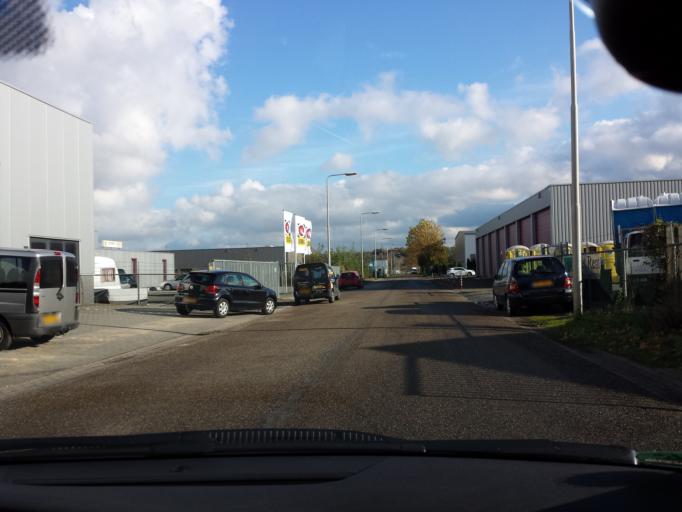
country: NL
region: Limburg
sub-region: Gemeente Kerkrade
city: Kerkrade
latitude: 50.8952
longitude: 6.0667
